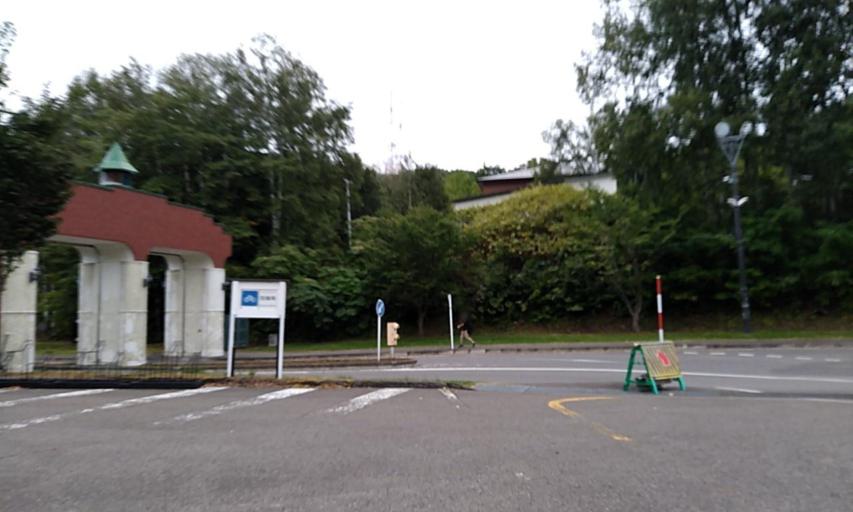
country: JP
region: Hokkaido
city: Abashiri
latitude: 43.9975
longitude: 144.2285
